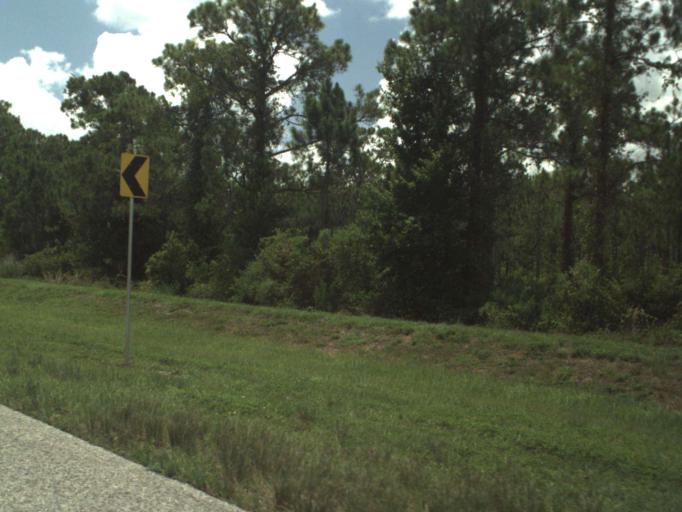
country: US
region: Florida
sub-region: Indian River County
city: Fellsmere
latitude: 27.6831
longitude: -80.8734
